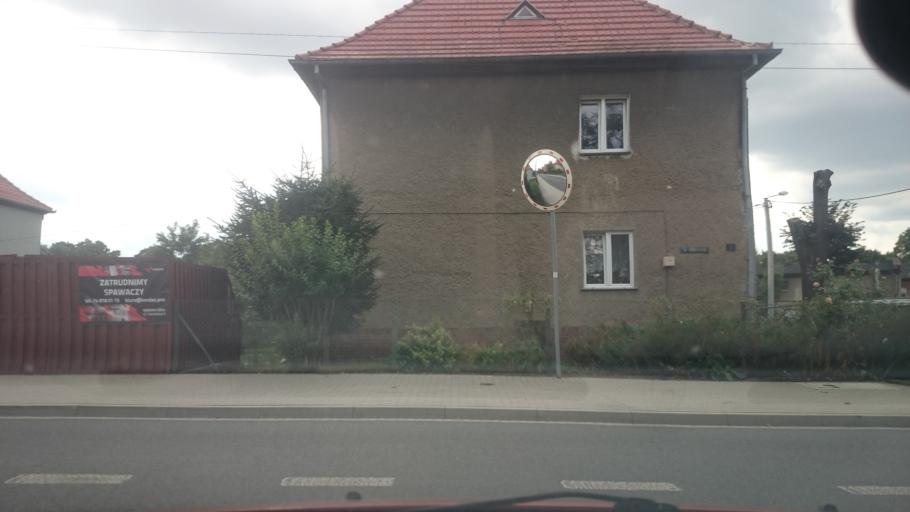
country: PL
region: Lower Silesian Voivodeship
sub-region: Powiat zabkowicki
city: Zabkowice Slaskie
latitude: 50.5945
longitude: 16.8166
